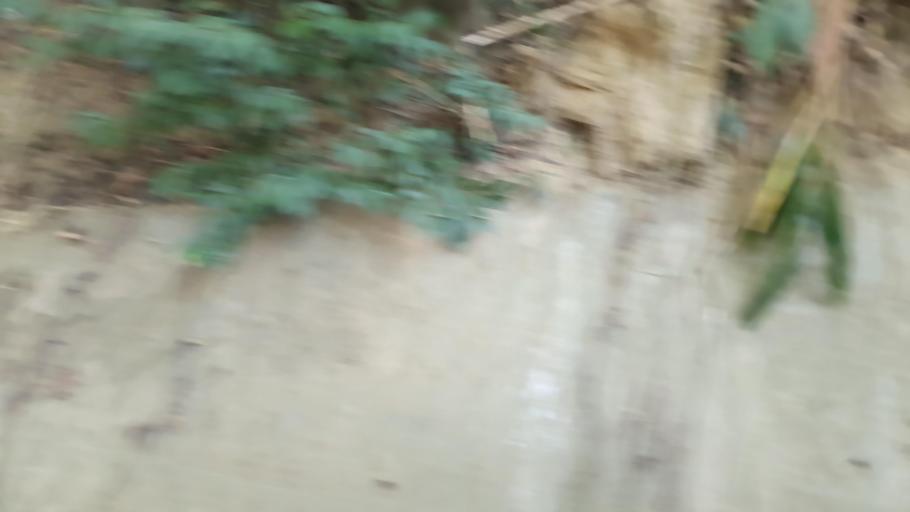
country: TW
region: Taiwan
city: Yujing
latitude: 23.0257
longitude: 120.3872
